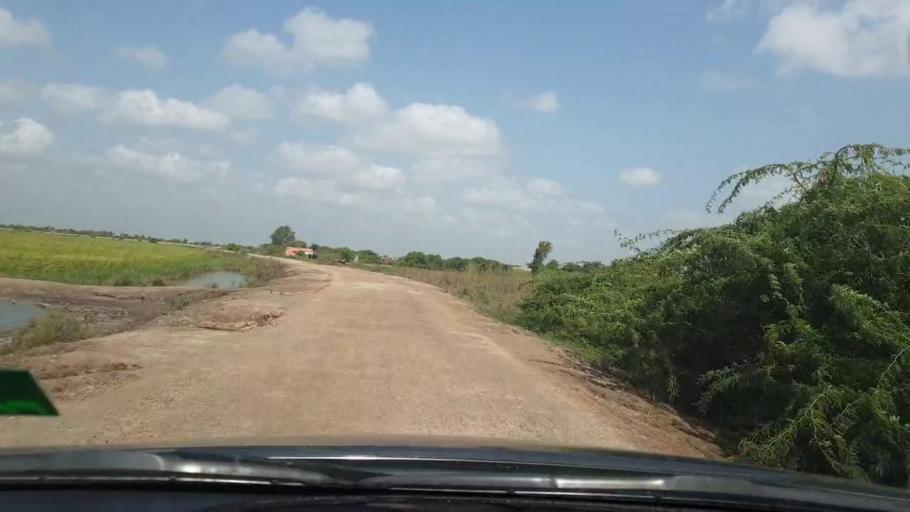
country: PK
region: Sindh
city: Tando Bago
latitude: 24.8646
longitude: 69.0573
